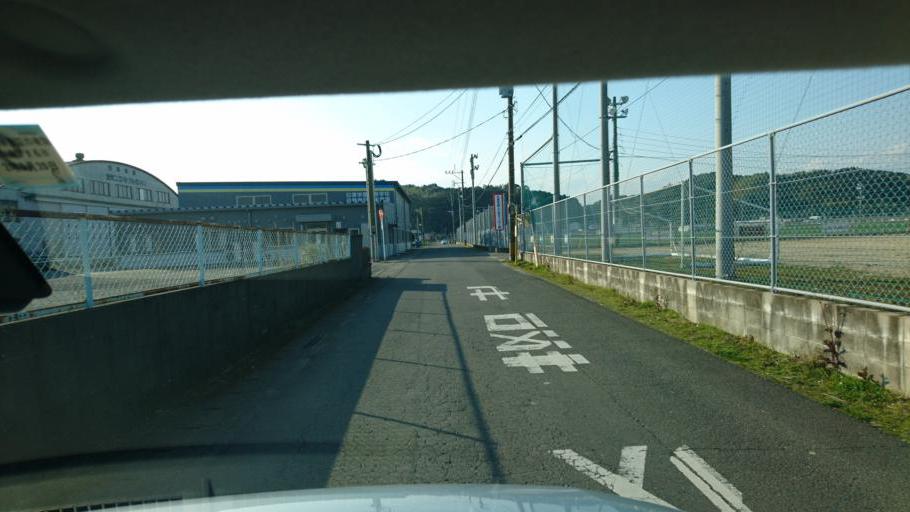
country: JP
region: Miyazaki
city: Miyazaki-shi
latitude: 32.0033
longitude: 131.4395
